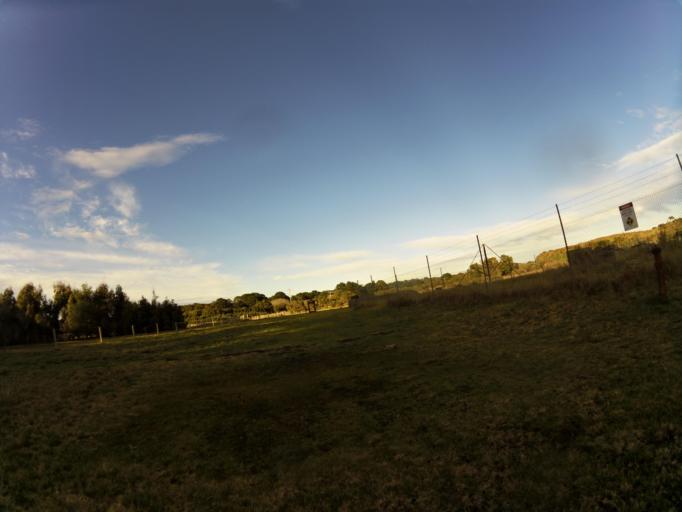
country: AU
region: Victoria
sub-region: Bass Coast
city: North Wonthaggi
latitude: -38.6050
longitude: 145.5744
